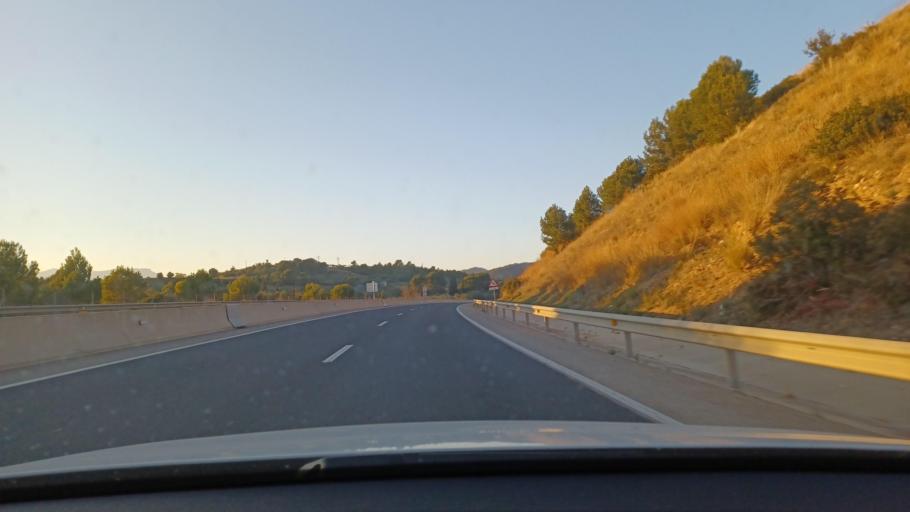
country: ES
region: Catalonia
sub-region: Provincia de Tarragona
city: Amposta
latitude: 40.7588
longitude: 0.5901
